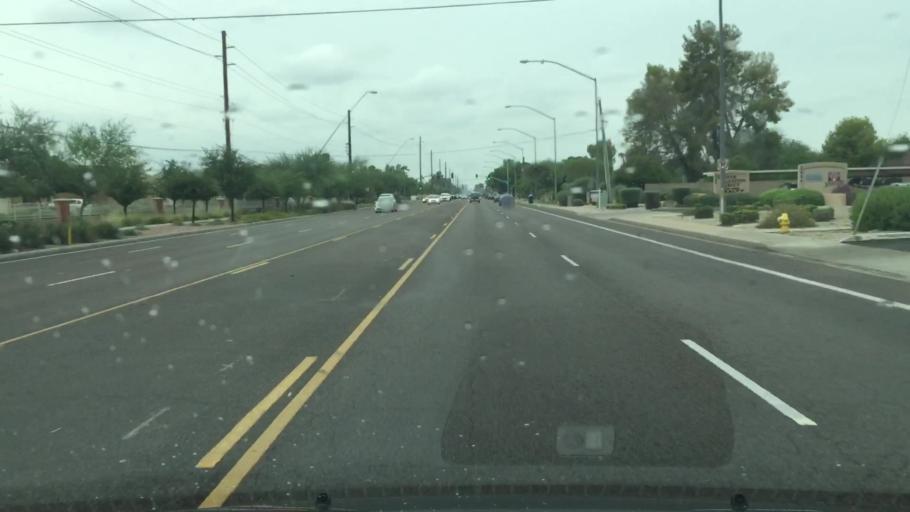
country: US
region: Arizona
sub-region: Maricopa County
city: Gilbert
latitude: 33.3937
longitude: -111.7772
